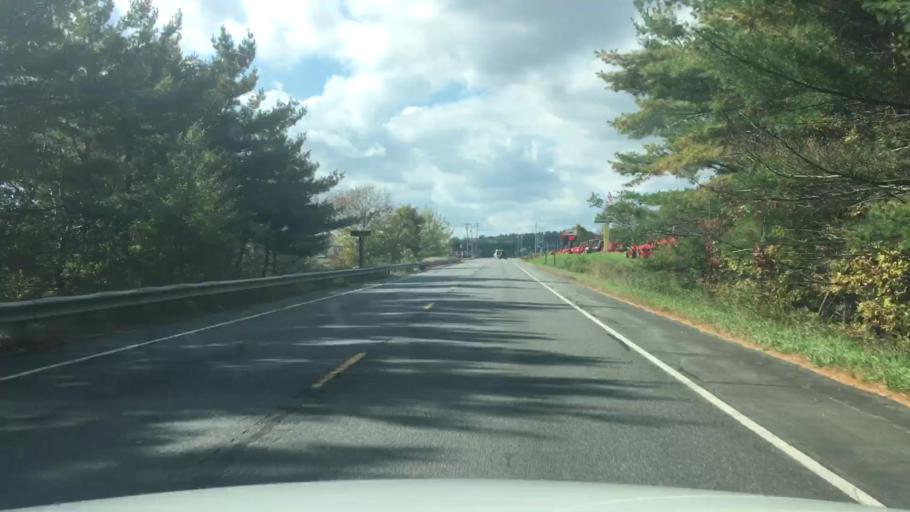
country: US
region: Maine
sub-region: Knox County
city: Union
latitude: 44.2171
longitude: -69.2800
